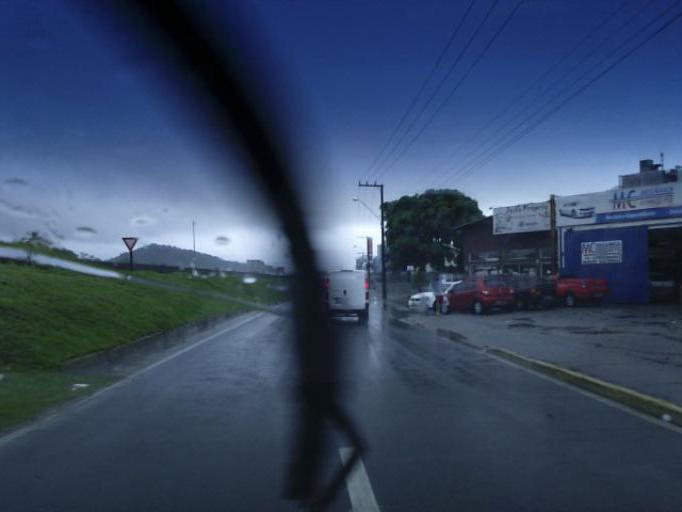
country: BR
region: Santa Catarina
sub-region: Itapema
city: Itapema
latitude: -27.1309
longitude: -48.6095
